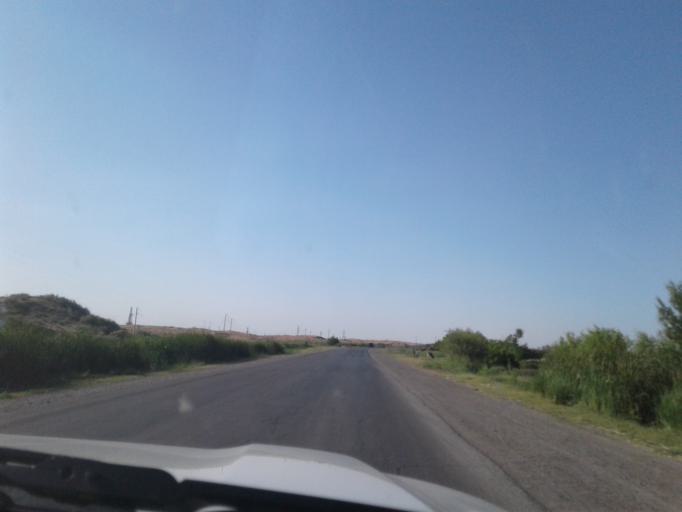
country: TM
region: Mary
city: Yoloeten
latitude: 37.1006
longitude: 62.4422
